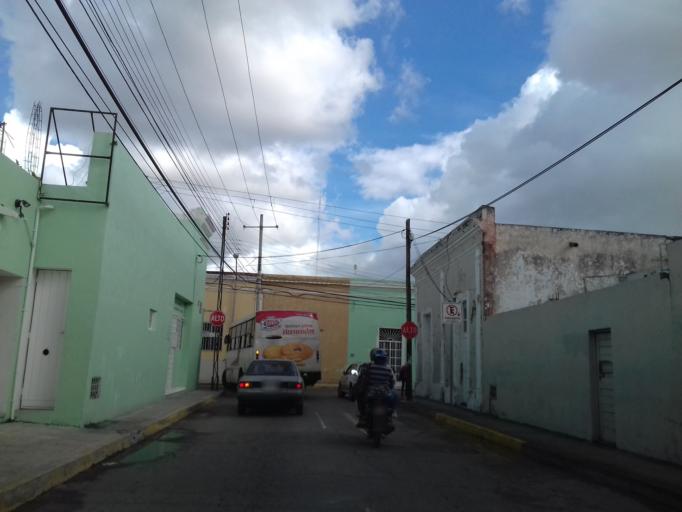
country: MX
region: Yucatan
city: Merida
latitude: 20.9718
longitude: -89.6287
